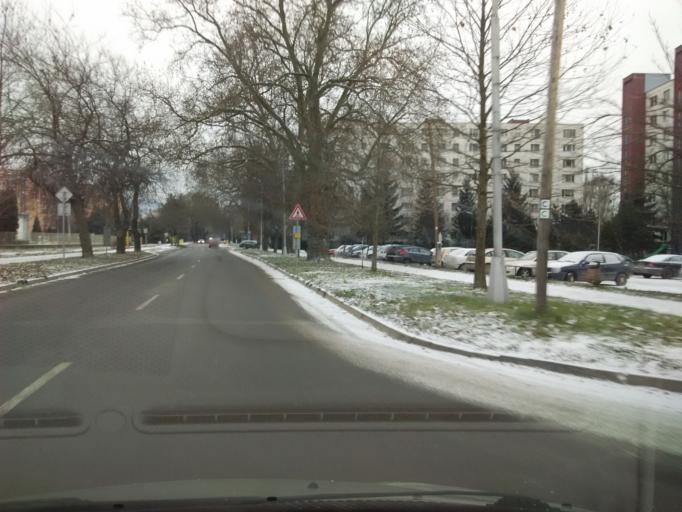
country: SK
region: Nitriansky
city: Zlate Moravce
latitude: 48.3875
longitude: 18.3779
